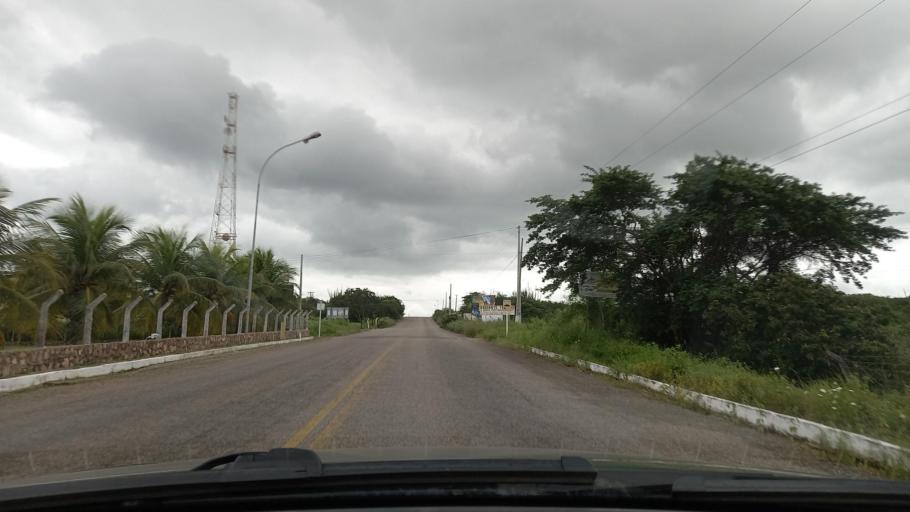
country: BR
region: Sergipe
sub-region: Caninde De Sao Francisco
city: Caninde de Sao Francisco
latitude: -9.6219
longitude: -37.7816
